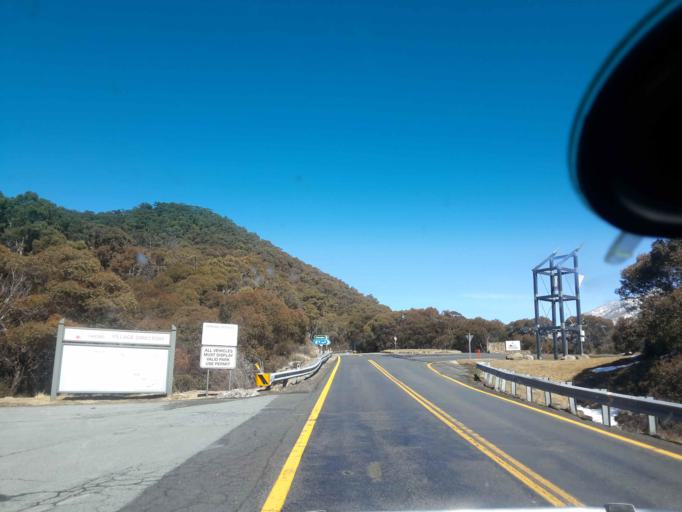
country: AU
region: New South Wales
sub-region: Snowy River
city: Jindabyne
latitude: -36.4996
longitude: 148.3174
